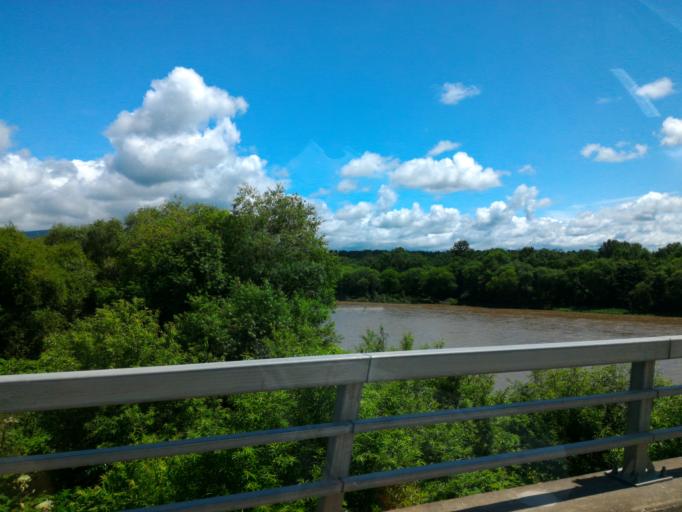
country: JP
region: Hokkaido
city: Nayoro
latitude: 44.5272
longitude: 142.3254
